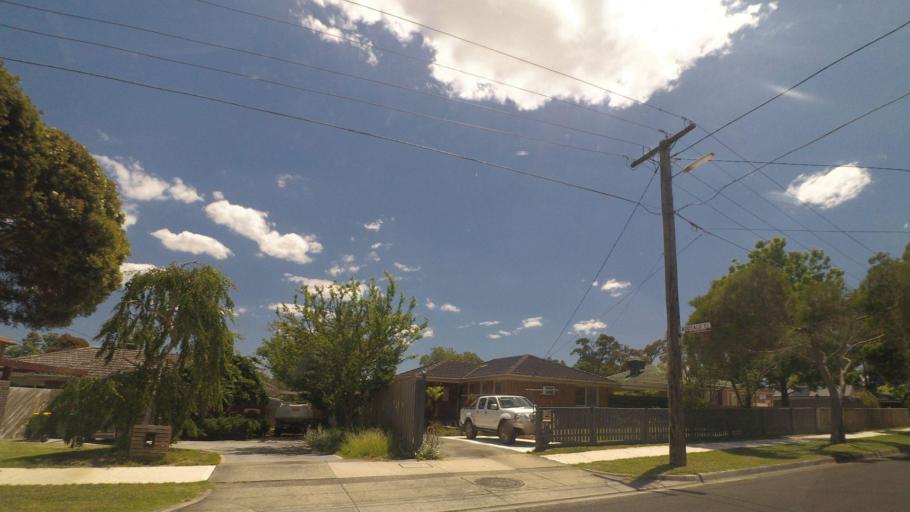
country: AU
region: Victoria
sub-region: Maroondah
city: Kilsyth South
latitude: -37.8107
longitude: 145.3272
